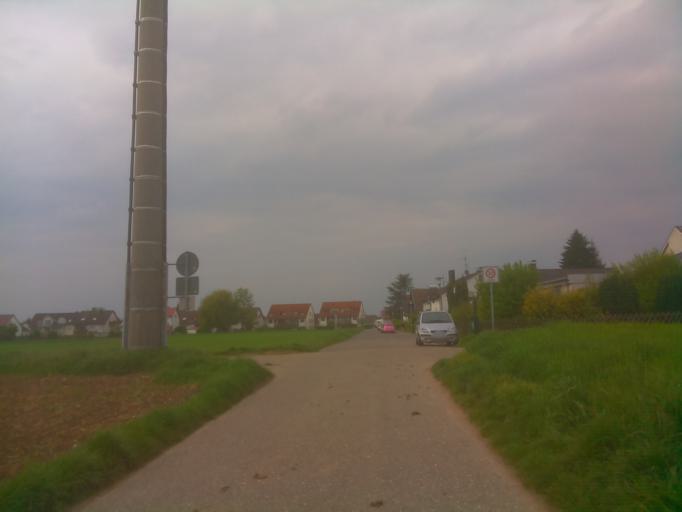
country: DE
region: Baden-Wuerttemberg
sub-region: Karlsruhe Region
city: Schriesheim
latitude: 49.4944
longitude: 8.6522
